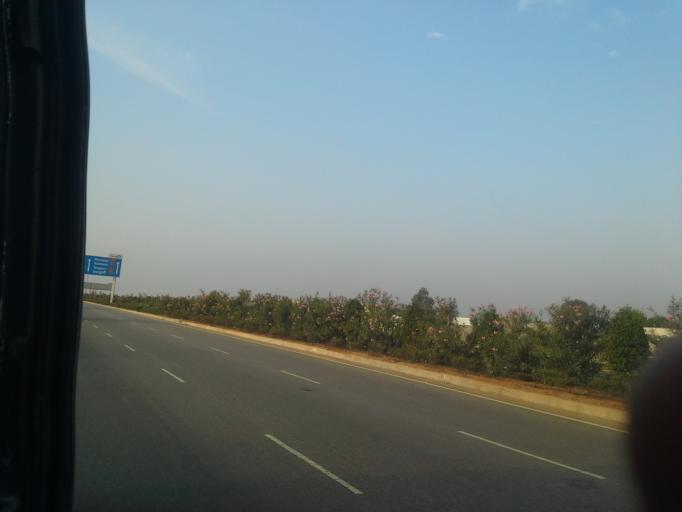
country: IN
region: Telangana
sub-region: Hyderabad
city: Hyderabad
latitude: 17.3358
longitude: 78.3680
